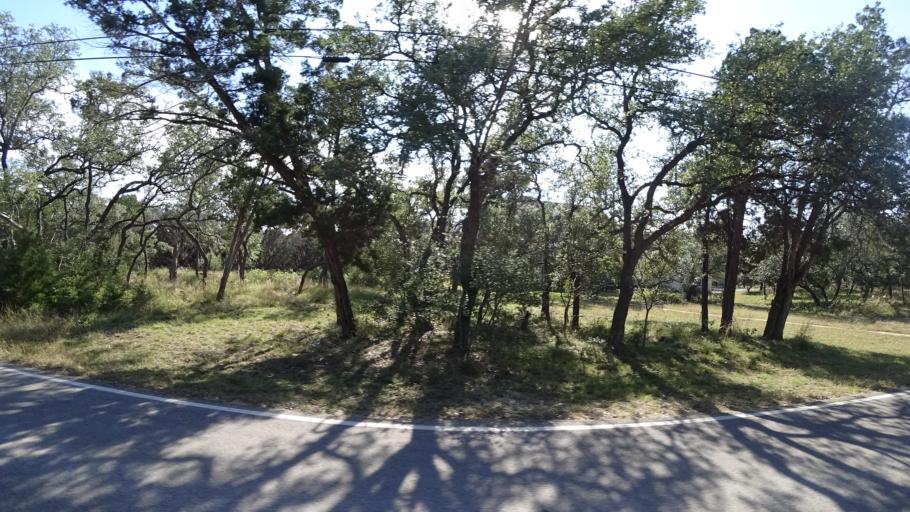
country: US
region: Texas
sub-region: Travis County
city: Barton Creek
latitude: 30.2276
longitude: -97.9082
